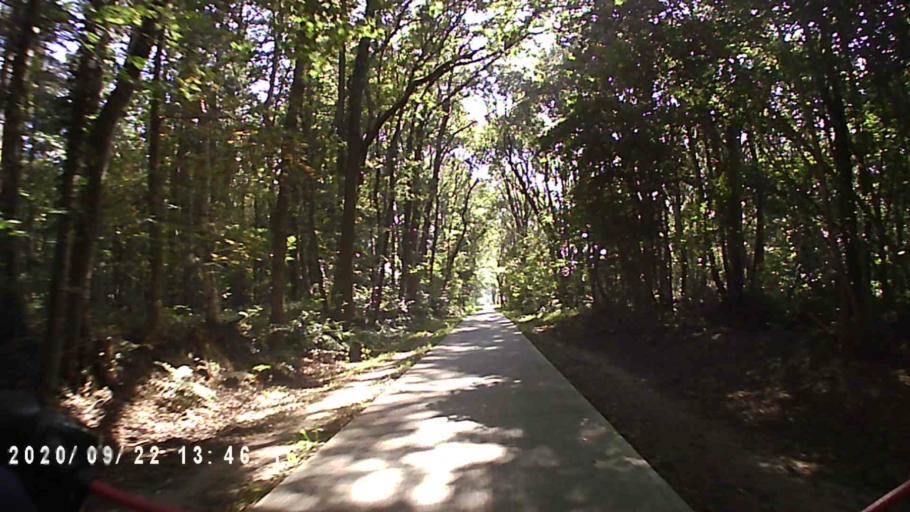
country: NL
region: Groningen
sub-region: Gemeente Leek
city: Leek
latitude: 53.1439
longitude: 6.4086
